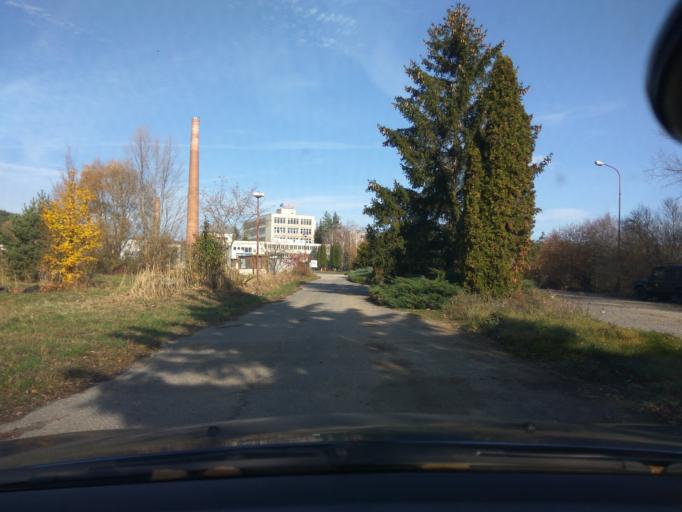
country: SK
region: Nitriansky
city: Brezova pod Bradlom
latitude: 48.6531
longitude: 17.5120
